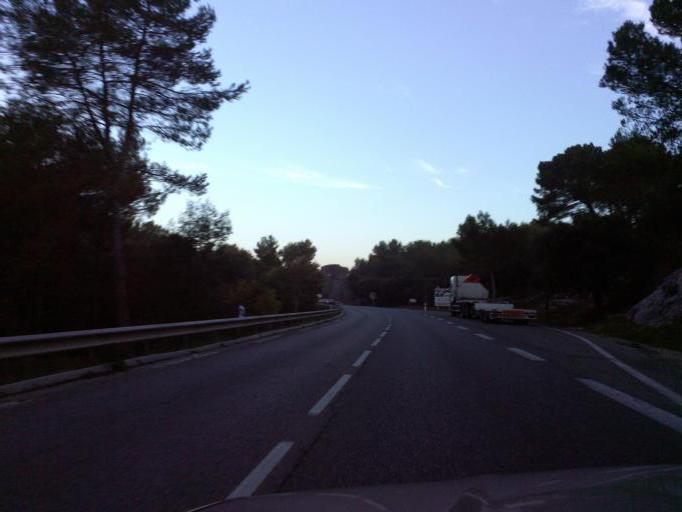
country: FR
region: Provence-Alpes-Cote d'Azur
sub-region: Departement des Bouches-du-Rhone
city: Lambesc
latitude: 43.6494
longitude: 5.2741
